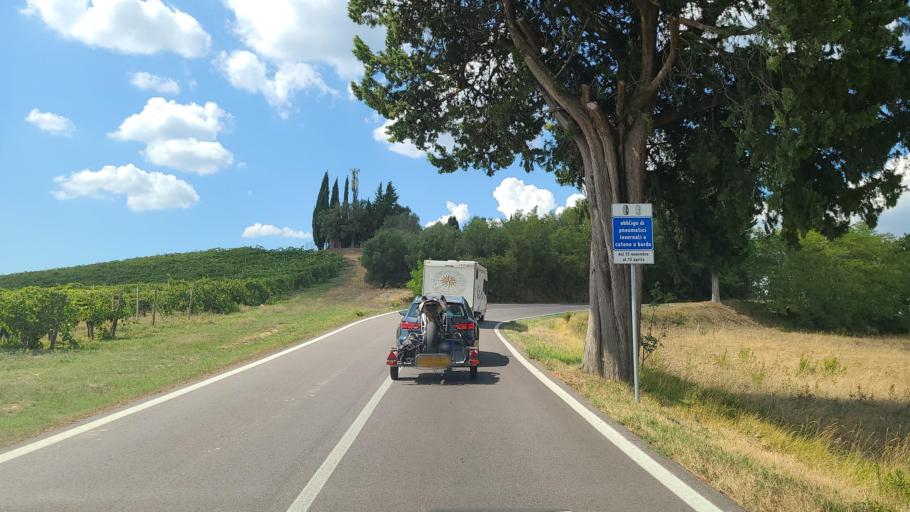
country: IT
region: Tuscany
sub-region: Provincia di Siena
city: Casole d'Elsa
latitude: 43.4038
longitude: 11.0142
